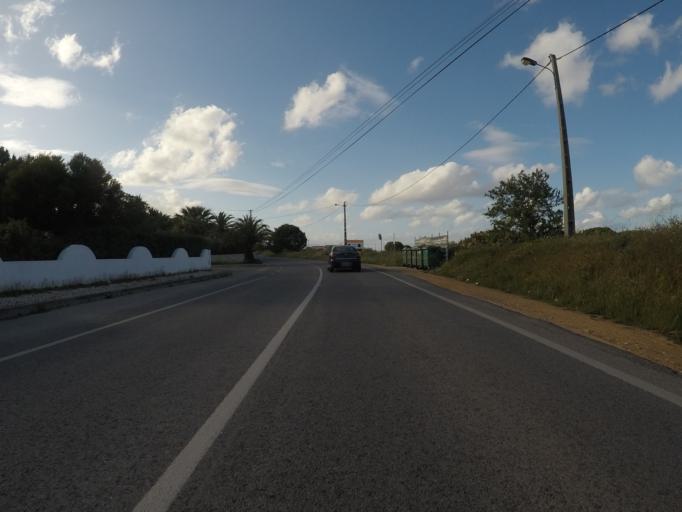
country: PT
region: Faro
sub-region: Lagoa
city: Carvoeiro
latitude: 37.0989
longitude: -8.4424
